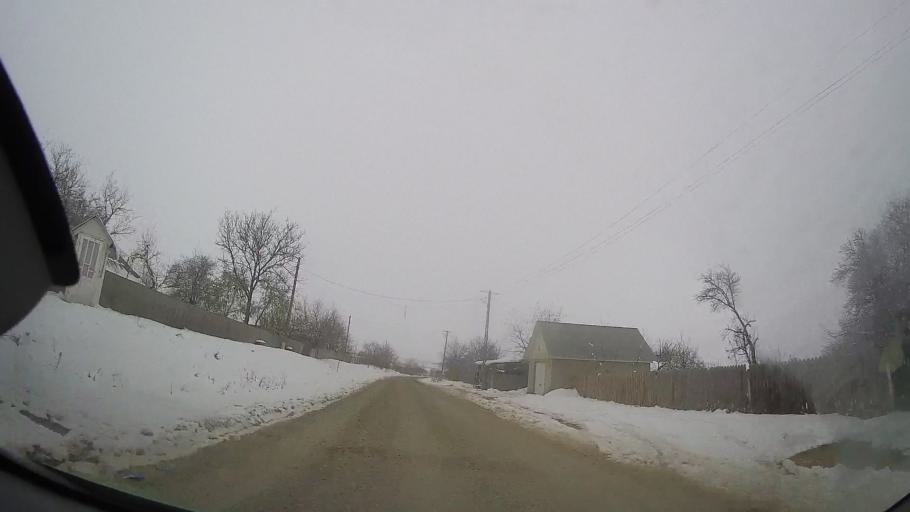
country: RO
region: Vaslui
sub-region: Comuna Todiresti
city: Todiresti
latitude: 46.8787
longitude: 27.3735
